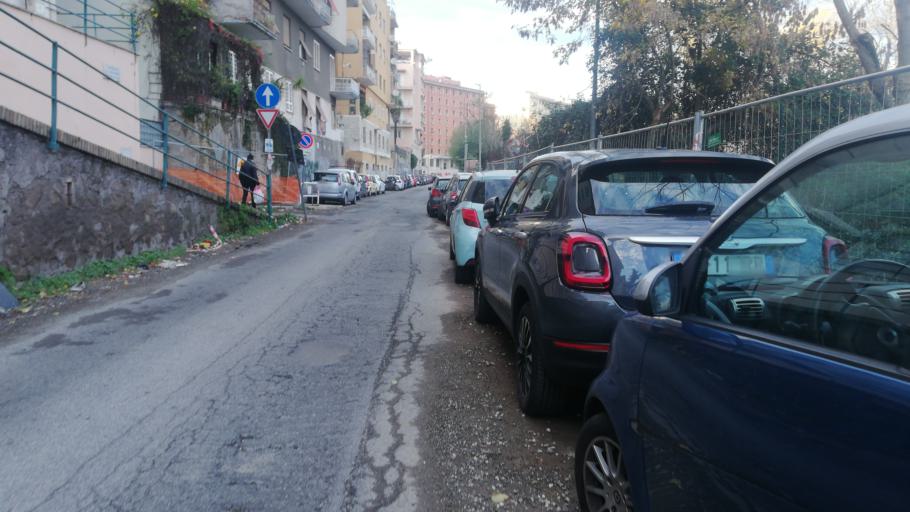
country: IT
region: Latium
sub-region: Citta metropolitana di Roma Capitale
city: Rome
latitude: 41.9310
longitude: 12.5288
